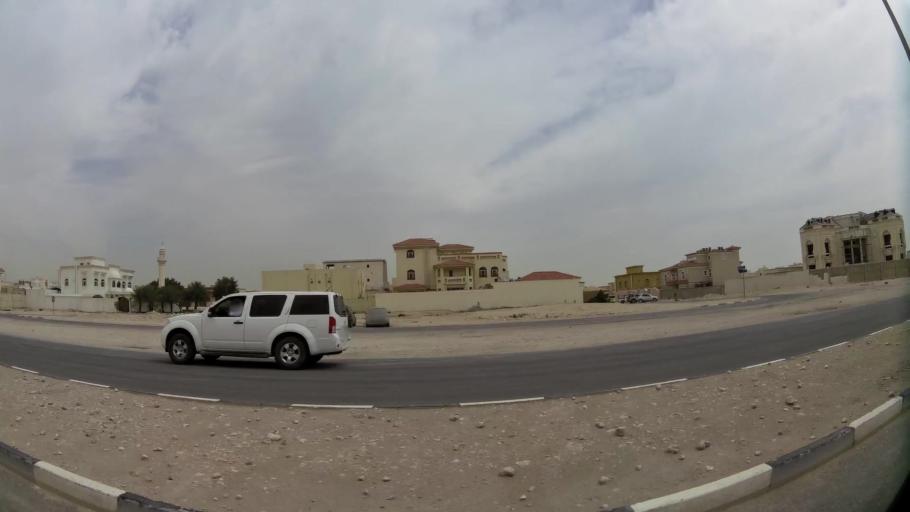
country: QA
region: Baladiyat ad Dawhah
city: Doha
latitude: 25.2187
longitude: 51.4879
